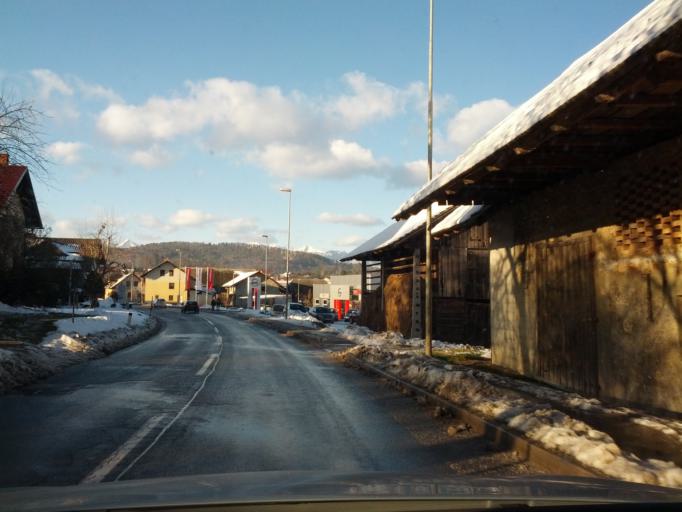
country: SI
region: Moravce
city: Moravce
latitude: 46.1314
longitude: 14.7483
